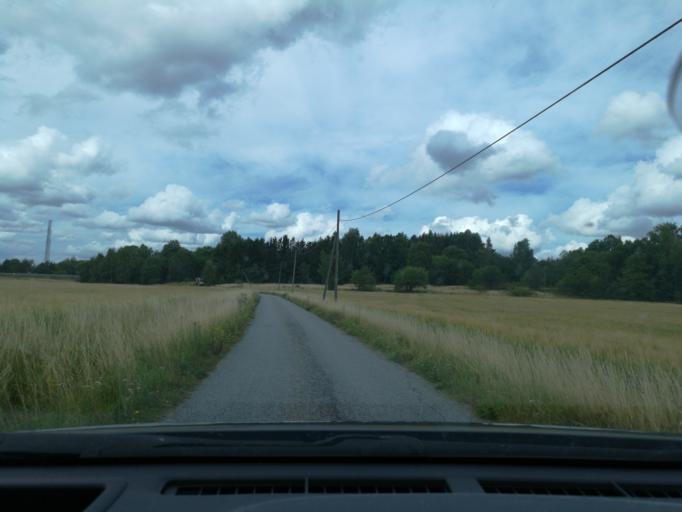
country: SE
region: Stockholm
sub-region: Sigtuna Kommun
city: Marsta
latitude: 59.6477
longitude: 17.8965
